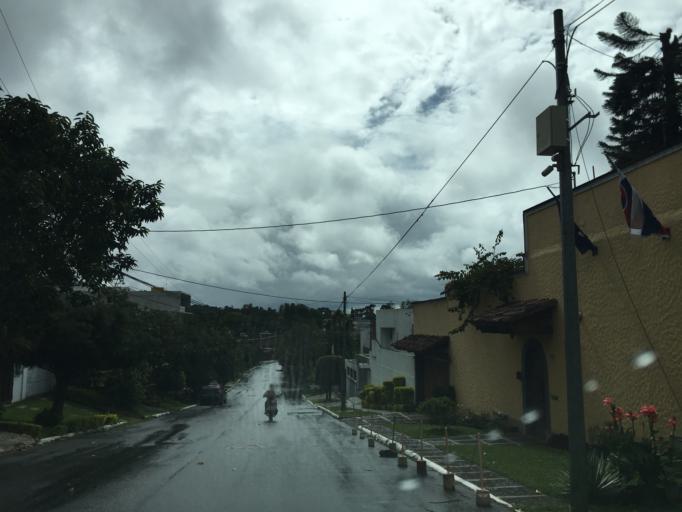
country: GT
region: Guatemala
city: Santa Catarina Pinula
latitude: 14.5836
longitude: -90.4882
